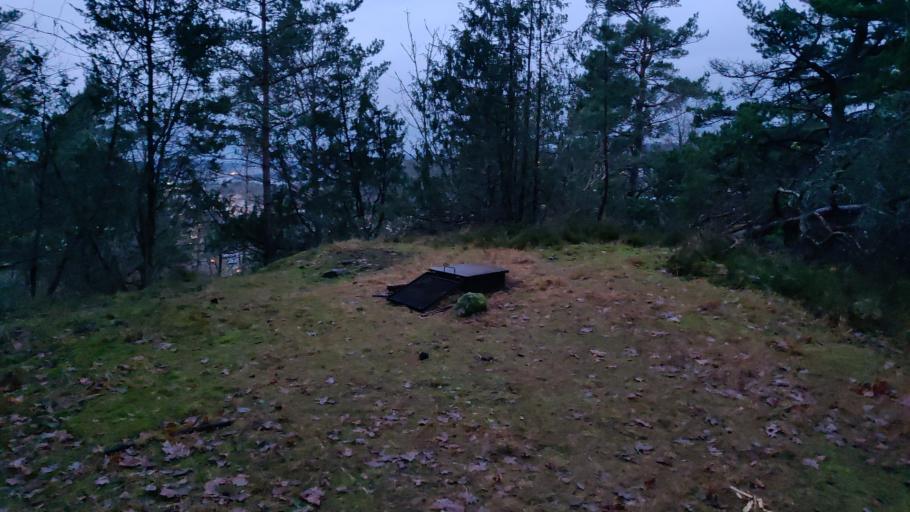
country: SE
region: Vaestra Goetaland
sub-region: Uddevalla Kommun
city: Uddevalla
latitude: 58.3419
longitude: 11.9334
